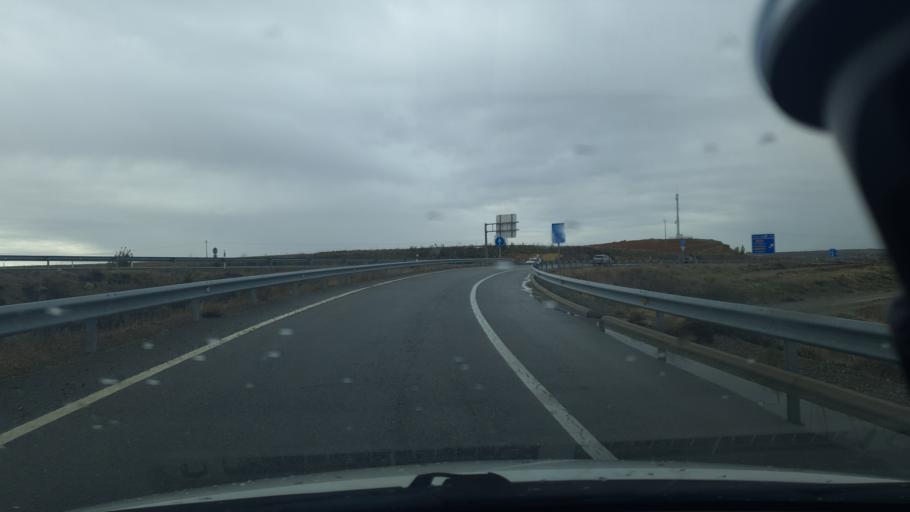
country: ES
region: Castille and Leon
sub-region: Provincia de Segovia
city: Encinillas
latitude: 40.9926
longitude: -4.1417
